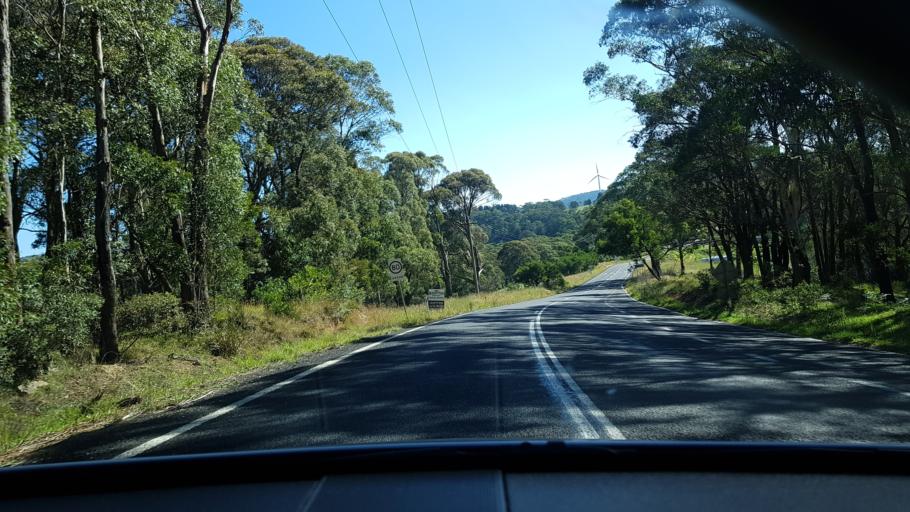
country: AU
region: New South Wales
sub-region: Lithgow
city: Bowenfels
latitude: -33.6396
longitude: 150.0628
